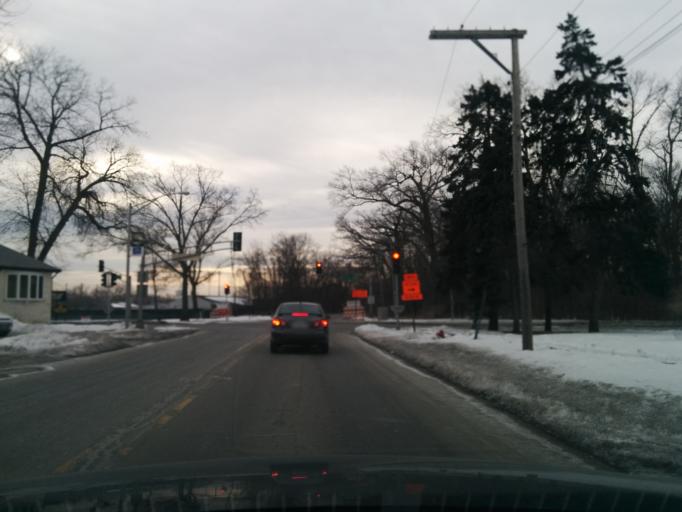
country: US
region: Illinois
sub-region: Cook County
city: River Grove
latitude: 41.9235
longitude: -87.8337
